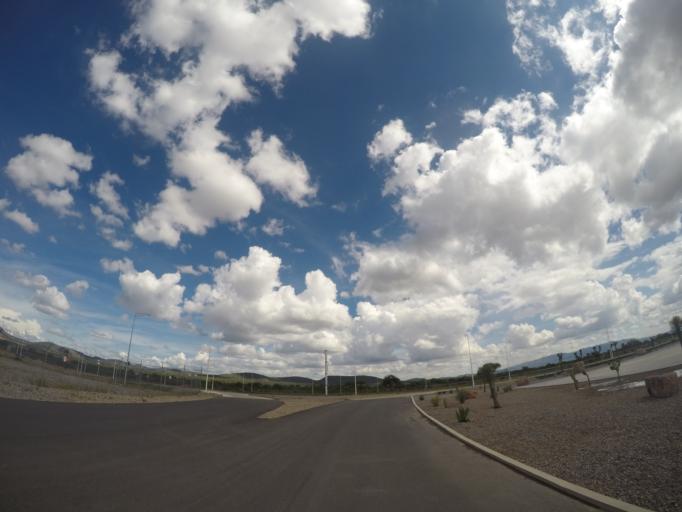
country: MX
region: San Luis Potosi
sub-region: Zaragoza
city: Cerro Gordo
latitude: 21.9644
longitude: -100.8434
